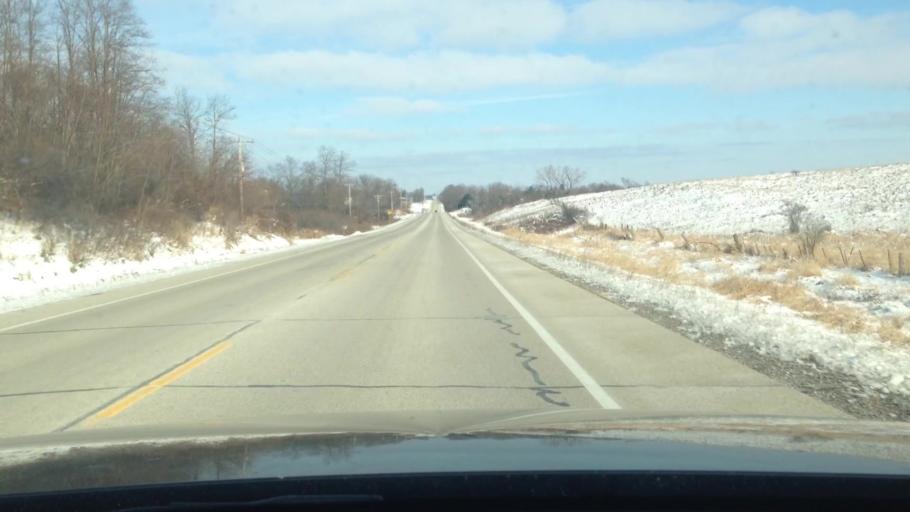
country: US
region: Wisconsin
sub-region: Walworth County
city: East Troy
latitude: 42.7023
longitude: -88.4050
